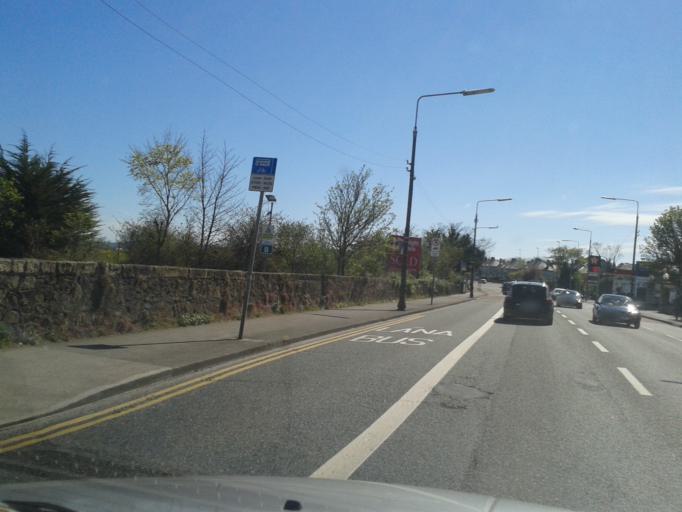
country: IE
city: Booterstown
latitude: 53.3131
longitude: -6.2020
